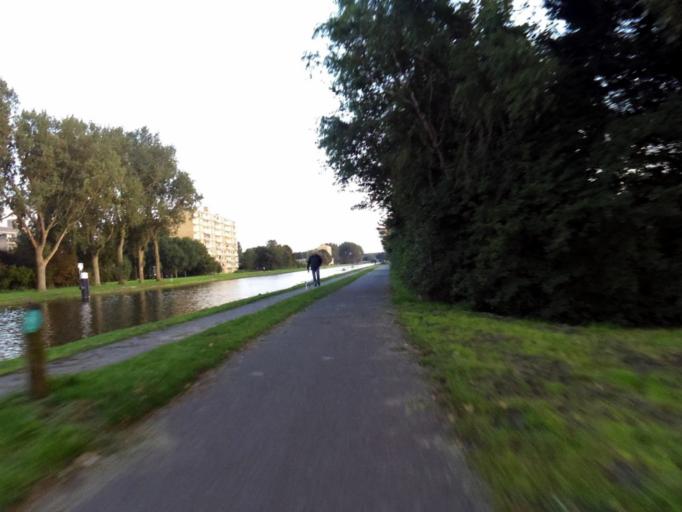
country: NL
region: South Holland
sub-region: Gemeente Voorschoten
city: Voorschoten
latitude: 52.1461
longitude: 4.4657
